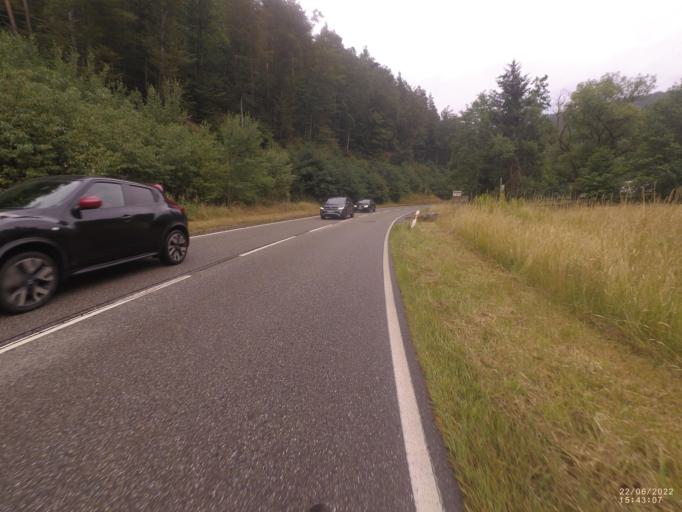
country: DE
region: Rheinland-Pfalz
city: Elmstein
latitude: 49.3468
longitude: 7.9559
